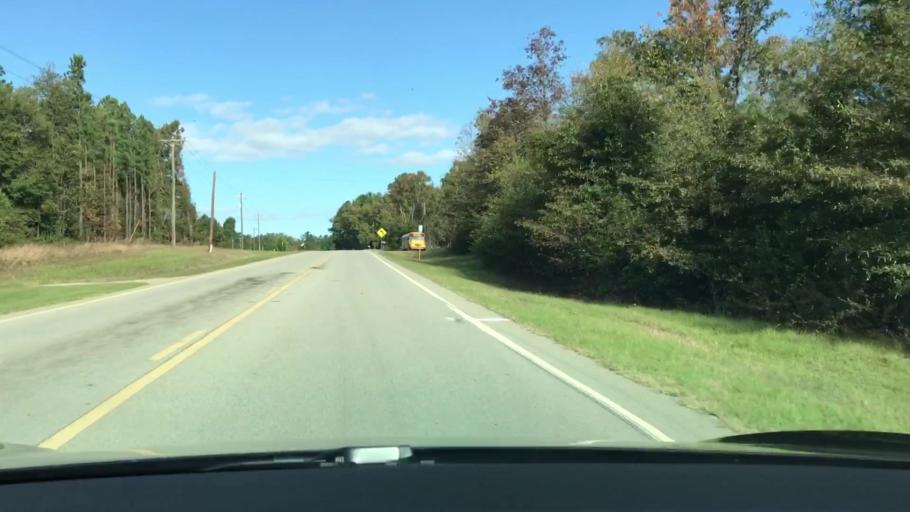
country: US
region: Georgia
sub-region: Jefferson County
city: Wrens
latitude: 33.1847
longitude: -82.4546
